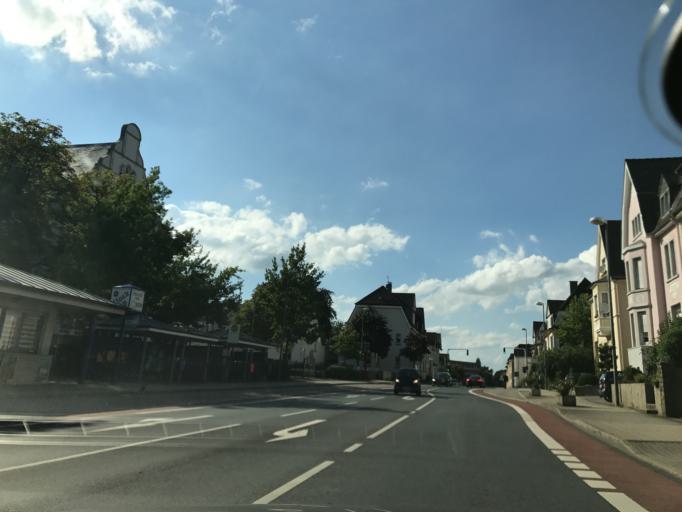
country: DE
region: North Rhine-Westphalia
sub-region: Regierungsbezirk Dusseldorf
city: Velbert
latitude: 51.3371
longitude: 7.0456
